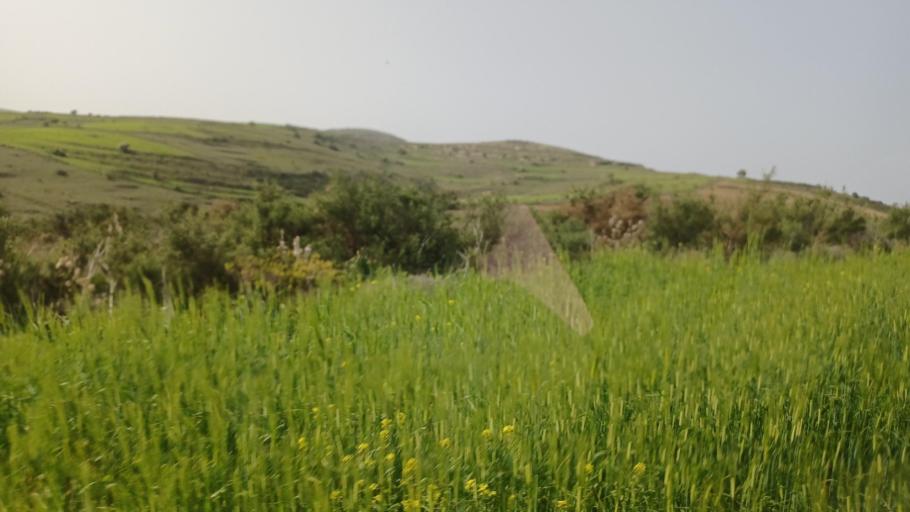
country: CY
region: Pafos
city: Polis
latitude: 35.0066
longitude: 32.3530
